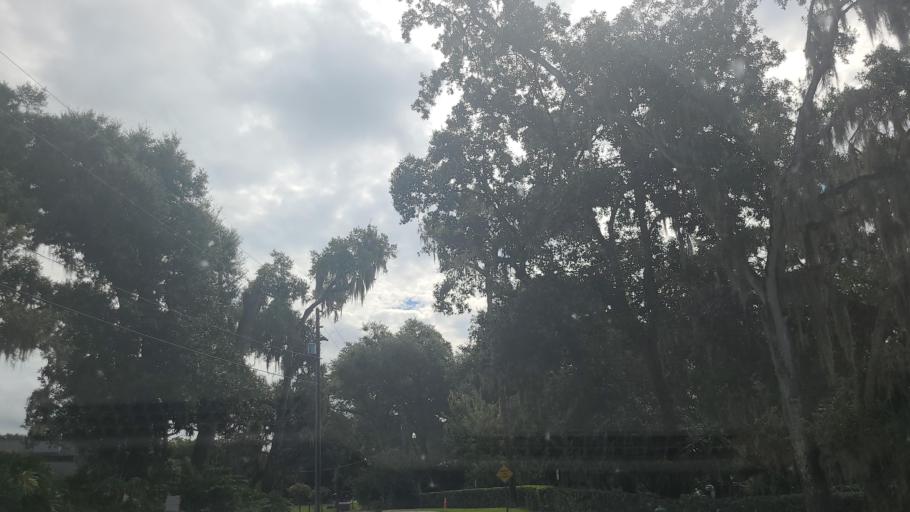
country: US
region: Florida
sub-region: Orange County
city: Lake Butler
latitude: 28.4980
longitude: -81.5414
